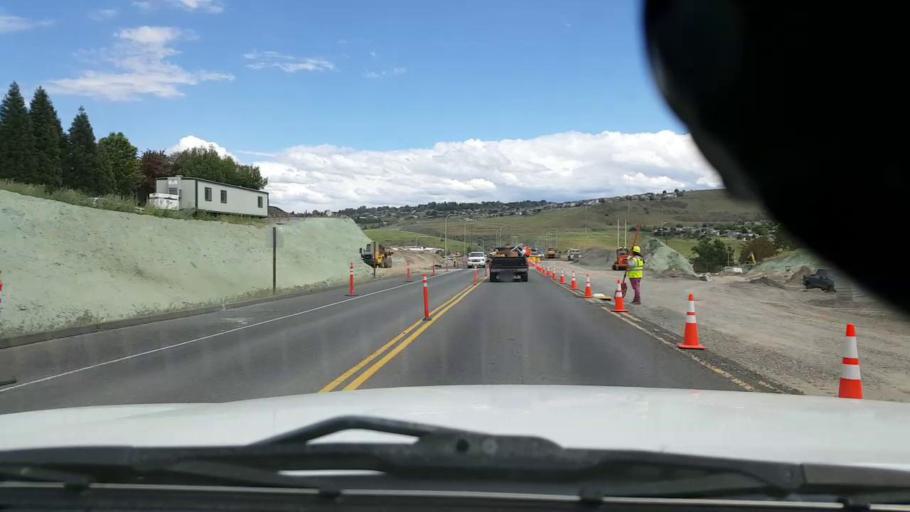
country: US
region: Washington
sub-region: Asotin County
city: West Clarkston-Highland
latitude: 46.3982
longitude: -117.0472
